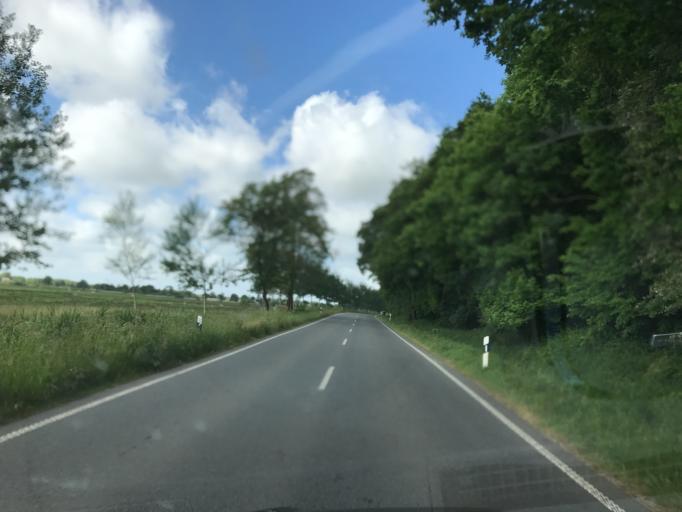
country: DE
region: Schleswig-Holstein
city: Kuden
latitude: 53.9637
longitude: 9.1802
